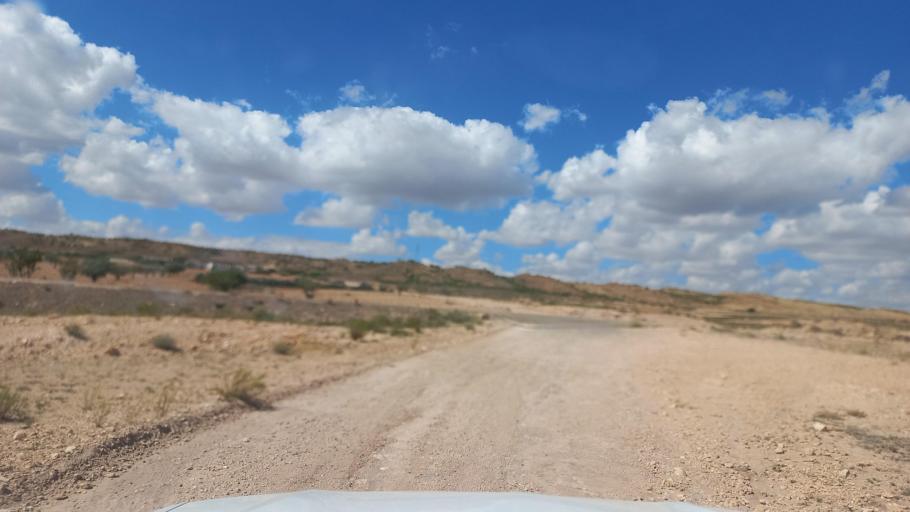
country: TN
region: Al Qasrayn
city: Sbiba
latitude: 35.3625
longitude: 9.0019
